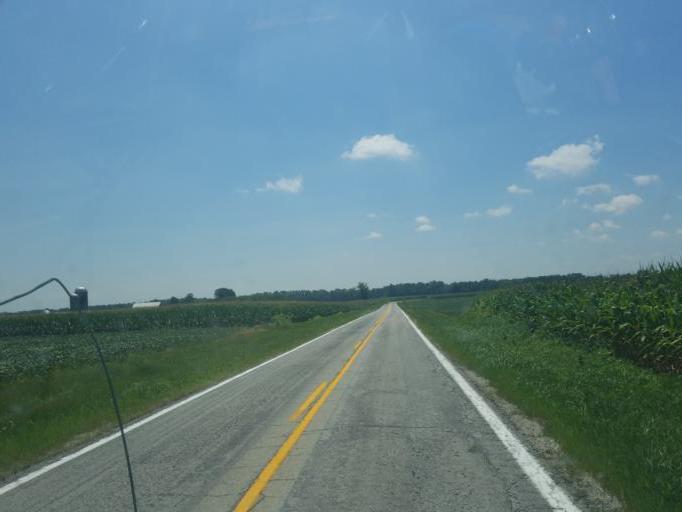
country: US
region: Ohio
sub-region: Allen County
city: Spencerville
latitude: 40.6706
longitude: -84.4160
